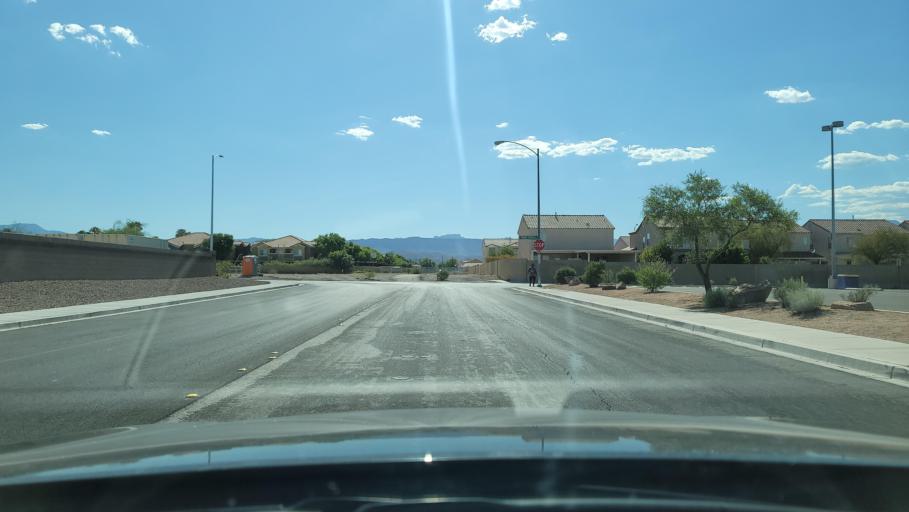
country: US
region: Nevada
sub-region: Clark County
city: Spring Valley
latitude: 36.0869
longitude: -115.2478
